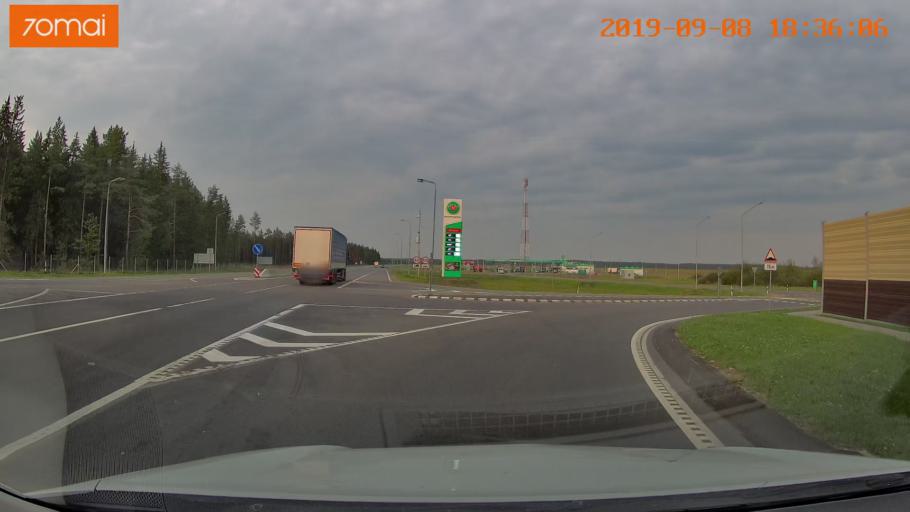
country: BY
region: Grodnenskaya
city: Iwye
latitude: 53.8922
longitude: 25.7945
